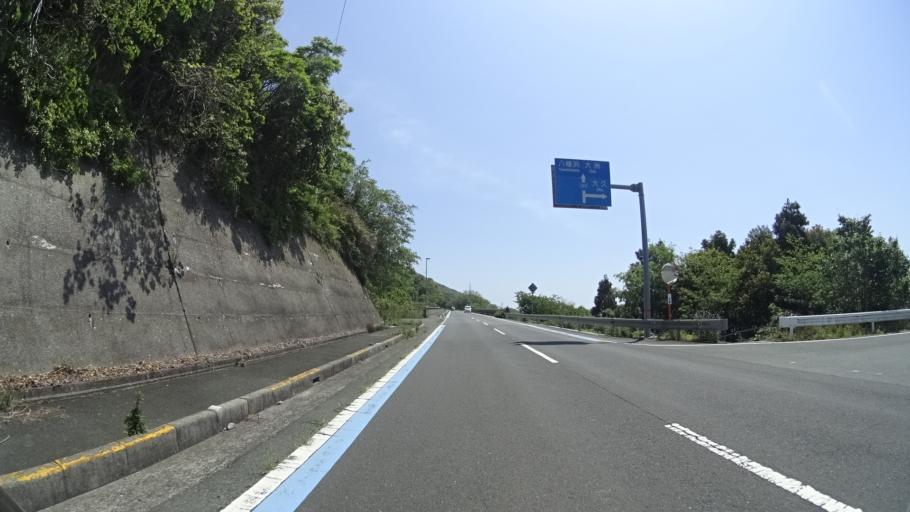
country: JP
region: Ehime
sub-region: Nishiuwa-gun
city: Ikata-cho
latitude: 33.4196
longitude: 132.1902
